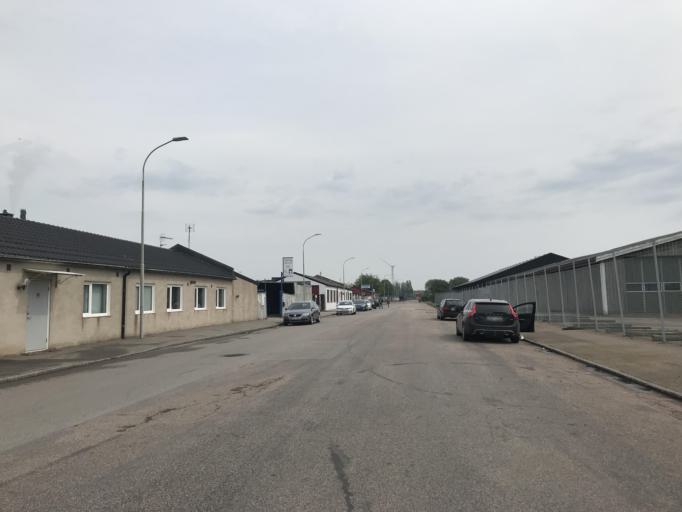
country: SE
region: Skane
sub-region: Landskrona
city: Landskrona
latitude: 55.8667
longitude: 12.8446
